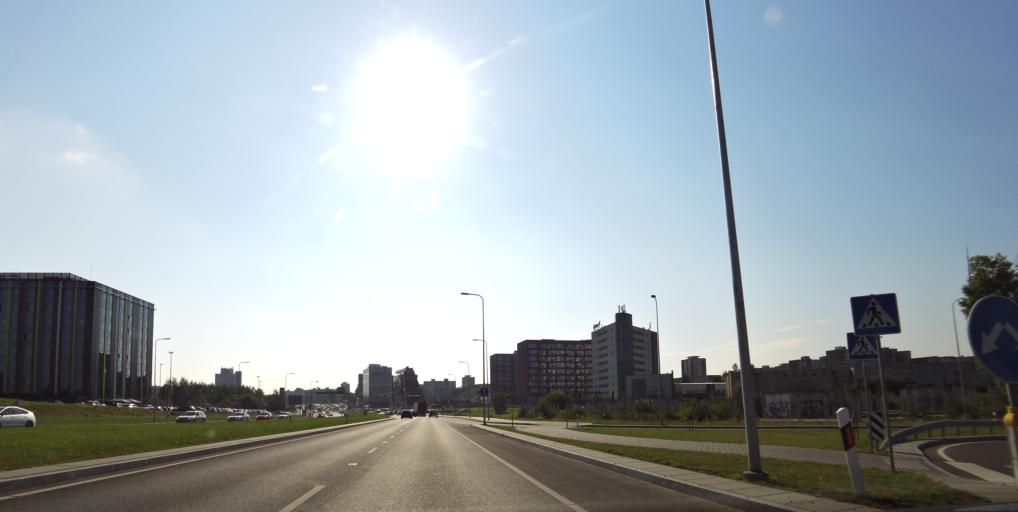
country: LT
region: Vilnius County
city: Justiniskes
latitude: 54.7002
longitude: 25.2088
